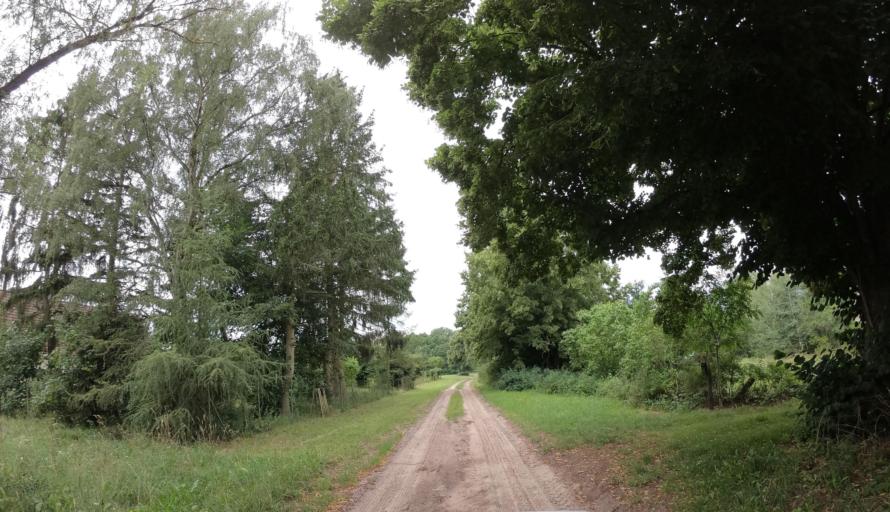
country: PL
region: West Pomeranian Voivodeship
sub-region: Powiat goleniowski
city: Przybiernow
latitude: 53.8251
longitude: 14.7373
